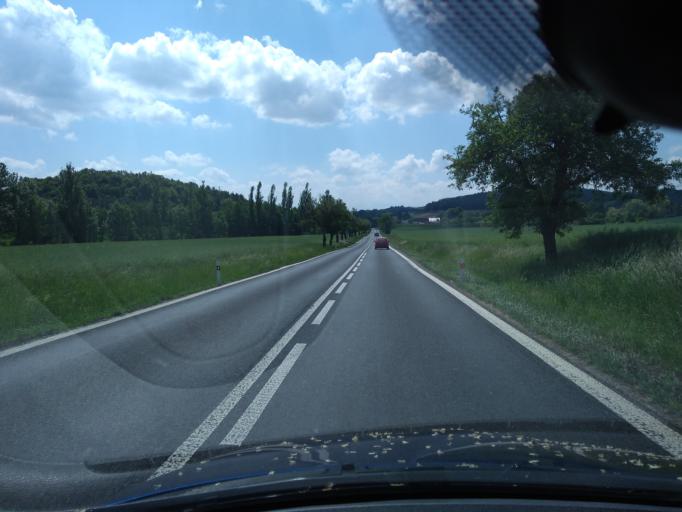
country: CZ
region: Plzensky
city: Svihov
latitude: 49.4546
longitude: 13.2894
